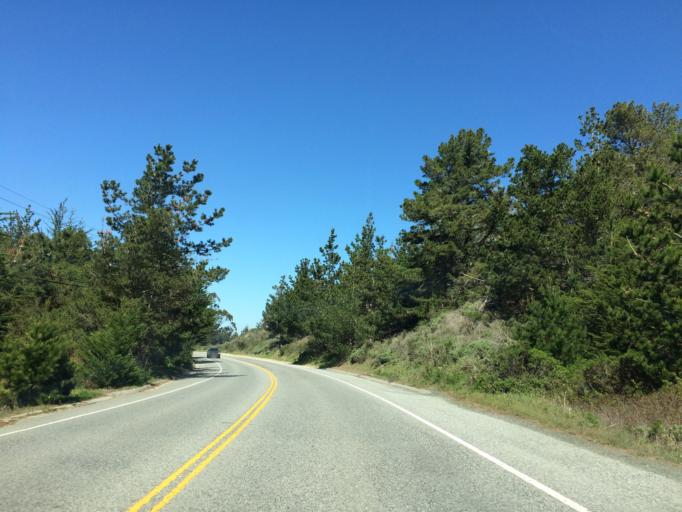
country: US
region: California
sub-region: San Mateo County
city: Half Moon Bay
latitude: 37.3433
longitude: -122.3946
